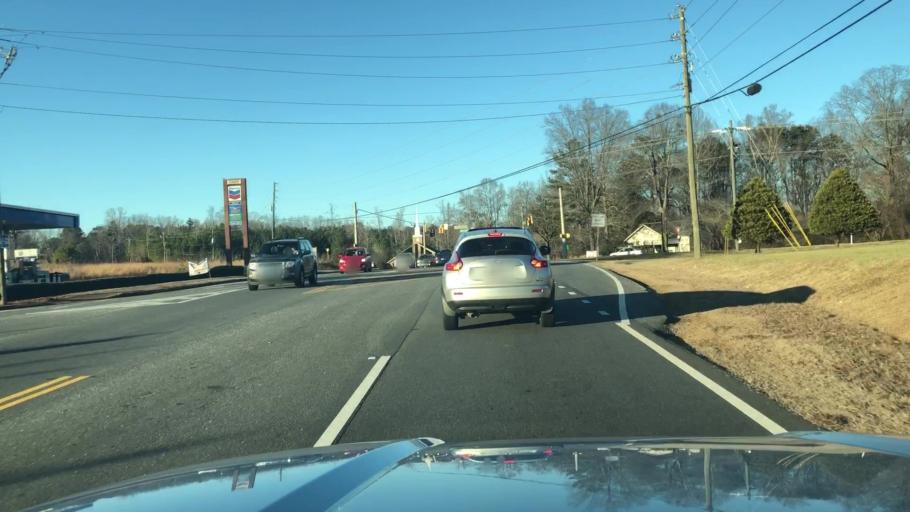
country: US
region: Georgia
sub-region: Cherokee County
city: Holly Springs
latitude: 34.2037
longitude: -84.5234
